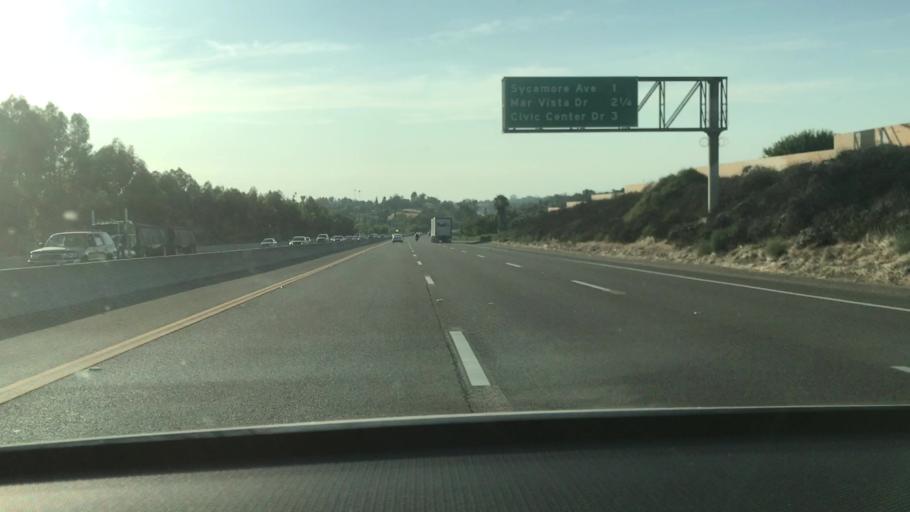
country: US
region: California
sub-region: San Diego County
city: Lake San Marcos
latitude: 33.1543
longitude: -117.2030
